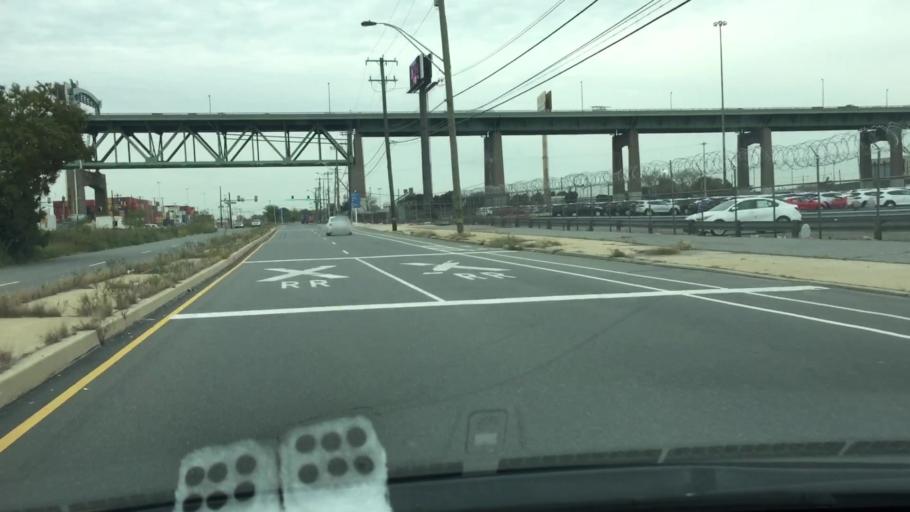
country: US
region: New Jersey
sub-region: Camden County
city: Camden
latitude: 39.9095
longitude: -75.1389
